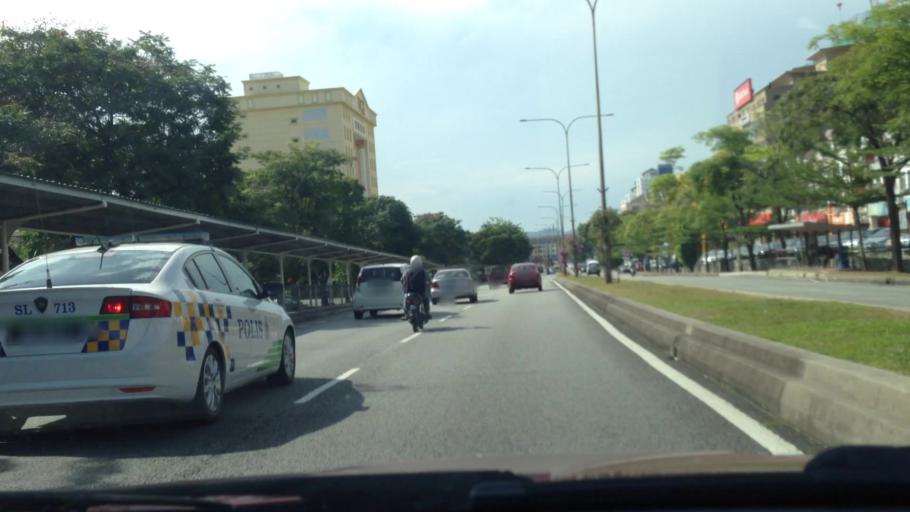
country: MY
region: Selangor
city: Subang Jaya
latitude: 3.0500
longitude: 101.5853
